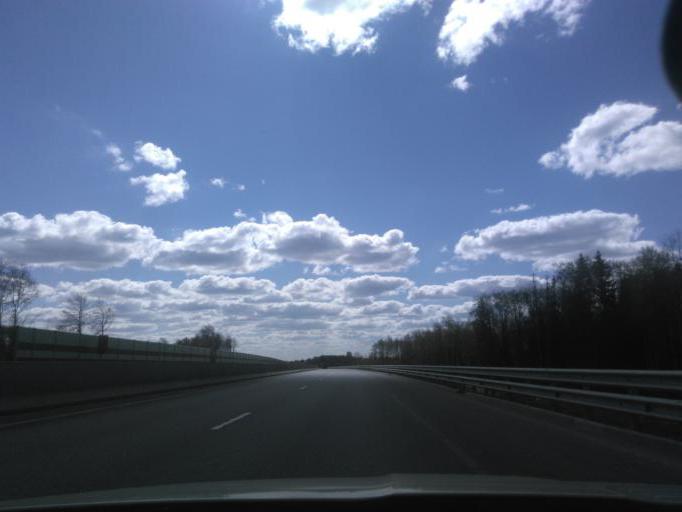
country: RU
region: Moskovskaya
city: Lozhki
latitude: 56.1138
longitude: 37.1203
